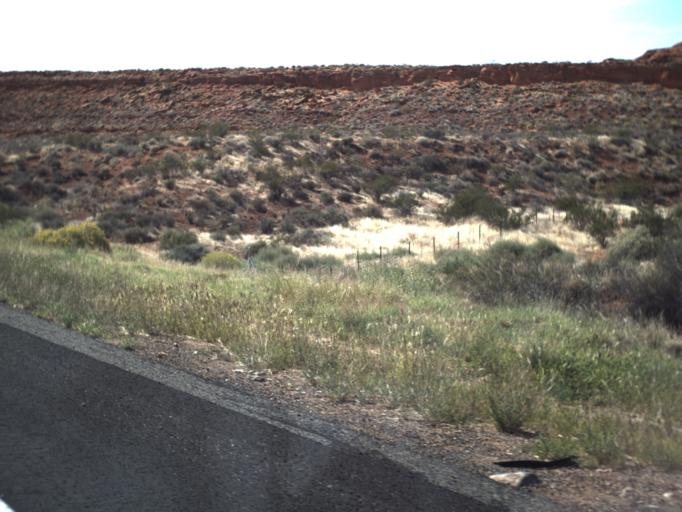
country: US
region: Utah
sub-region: Washington County
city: Washington
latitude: 37.1641
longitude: -113.4585
